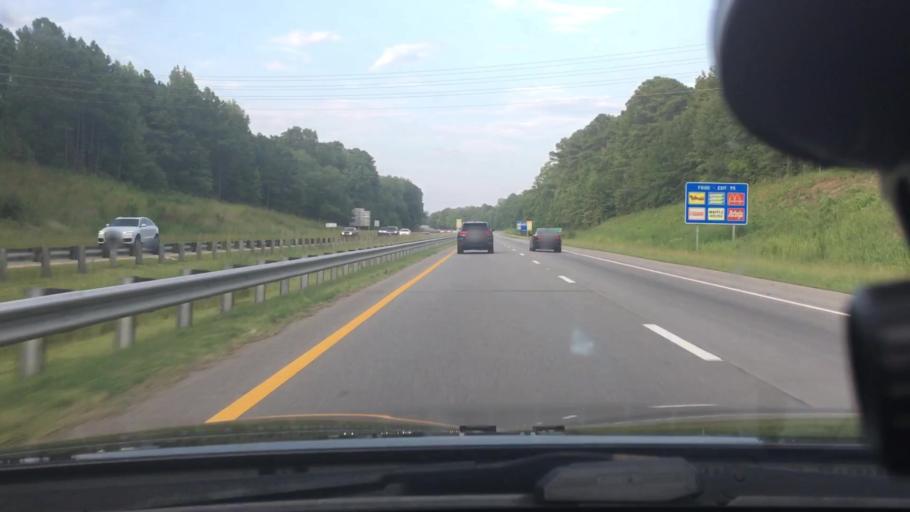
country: US
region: North Carolina
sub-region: Wake County
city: Apex
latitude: 35.7075
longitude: -78.8506
